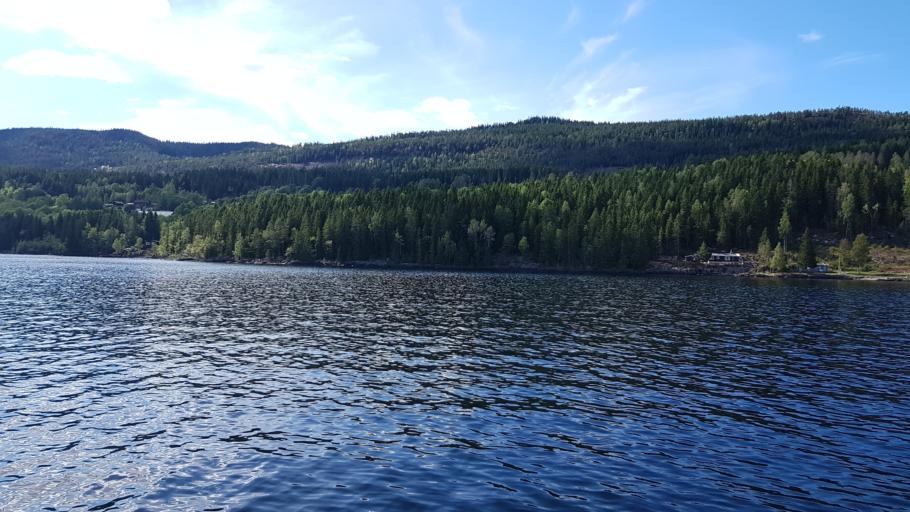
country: NO
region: Akershus
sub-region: Hurdal
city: Hurdal
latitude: 60.5423
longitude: 11.1988
